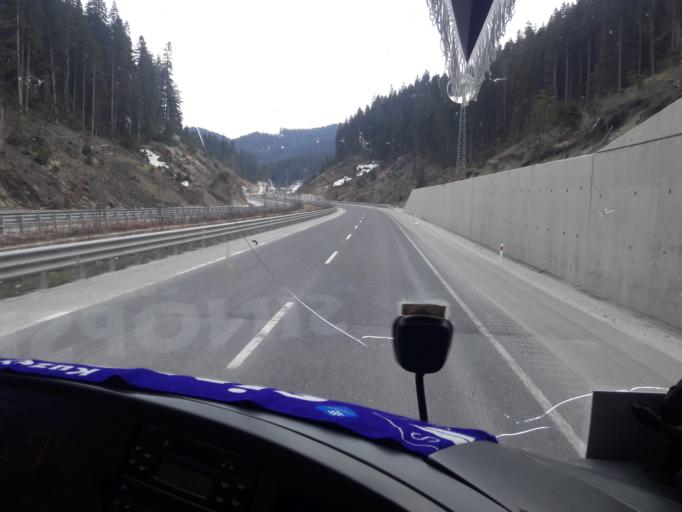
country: TR
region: Kastamonu
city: Kuzyaka
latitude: 41.0967
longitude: 33.7494
